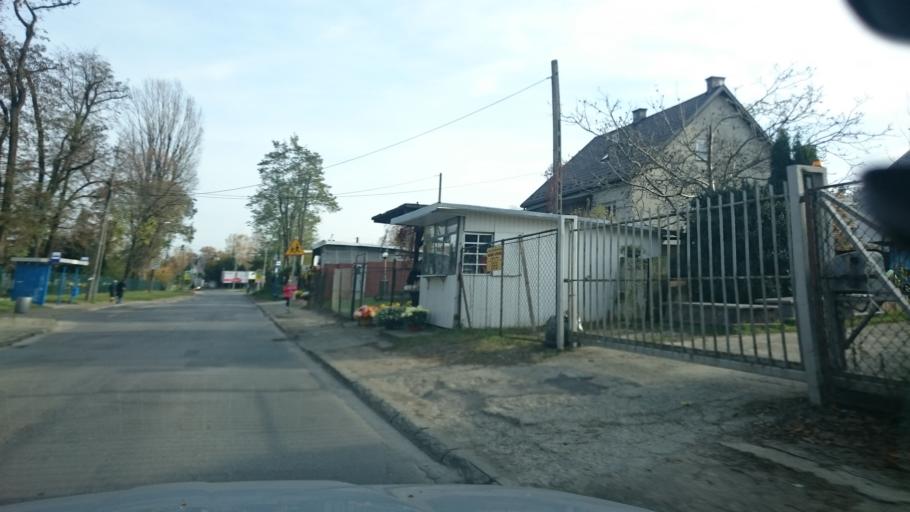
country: PL
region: Lesser Poland Voivodeship
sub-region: Powiat wielicki
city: Czarnochowice
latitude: 50.0220
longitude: 20.0066
